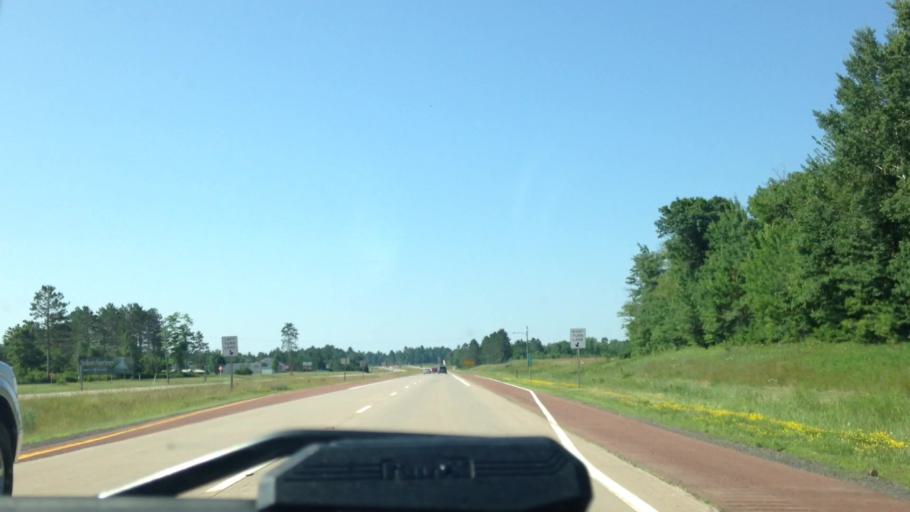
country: US
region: Wisconsin
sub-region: Douglas County
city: Lake Nebagamon
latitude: 46.3615
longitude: -91.8319
